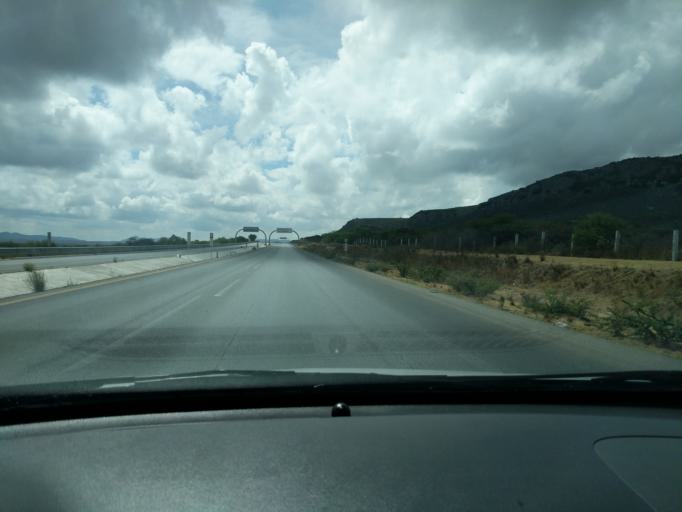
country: MX
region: Zacatecas
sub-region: Pinos
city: Santiago
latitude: 22.4014
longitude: -101.3789
